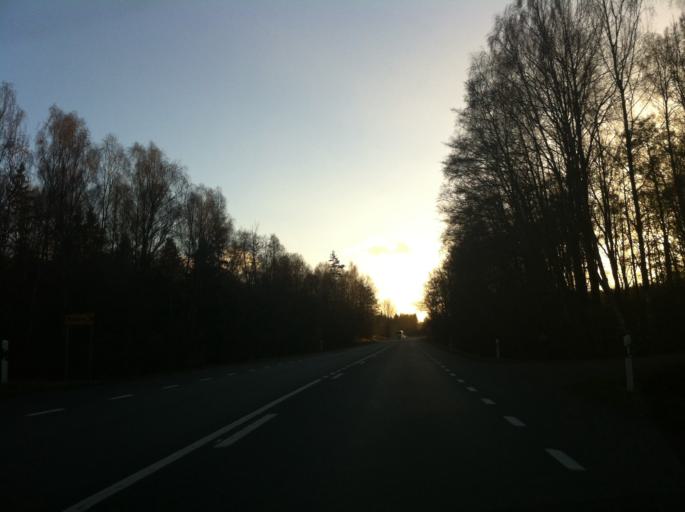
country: SE
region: Skane
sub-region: Hassleholms Kommun
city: Hassleholm
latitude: 56.1614
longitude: 13.8227
